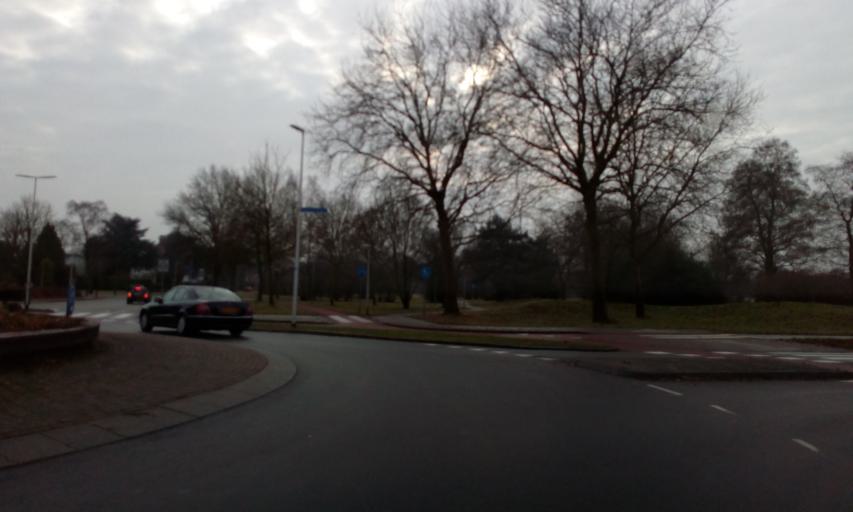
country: NL
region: North Holland
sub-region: Gemeente Bussum
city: Bussum
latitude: 52.2692
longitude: 5.1810
